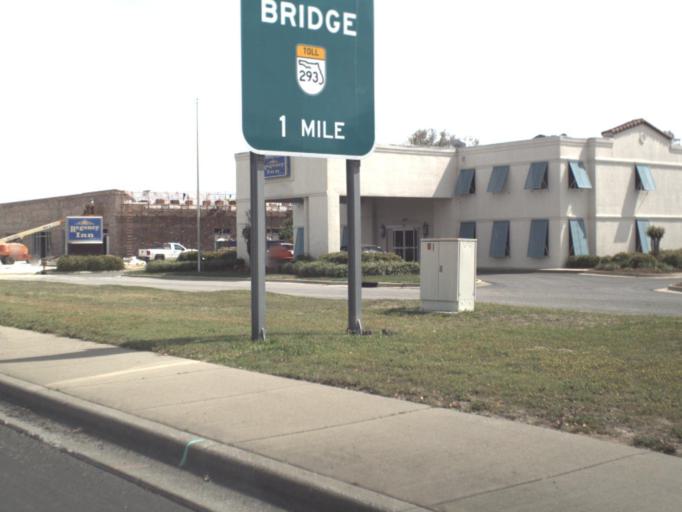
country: US
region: Florida
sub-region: Okaloosa County
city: Niceville
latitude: 30.4827
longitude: -86.4154
